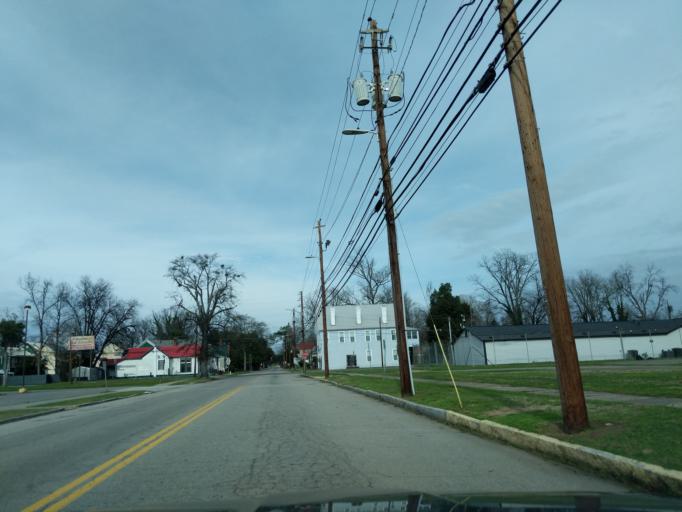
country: US
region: Georgia
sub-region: Richmond County
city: Augusta
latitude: 33.4663
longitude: -81.9591
